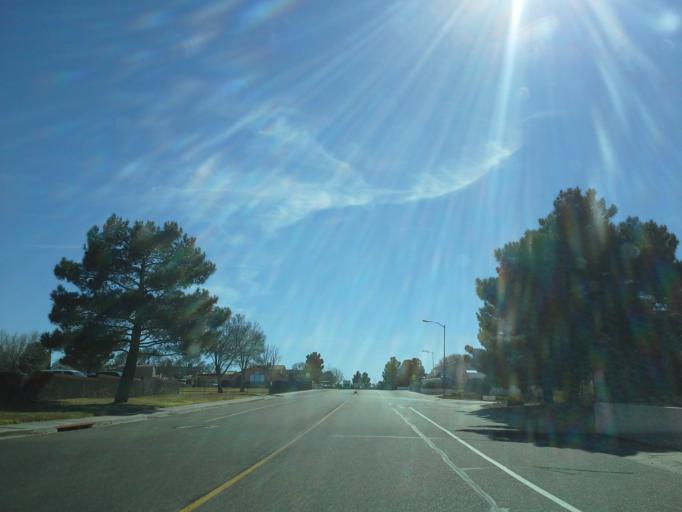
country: US
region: Arizona
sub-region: Coconino County
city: Page
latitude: 36.9312
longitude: -111.4612
